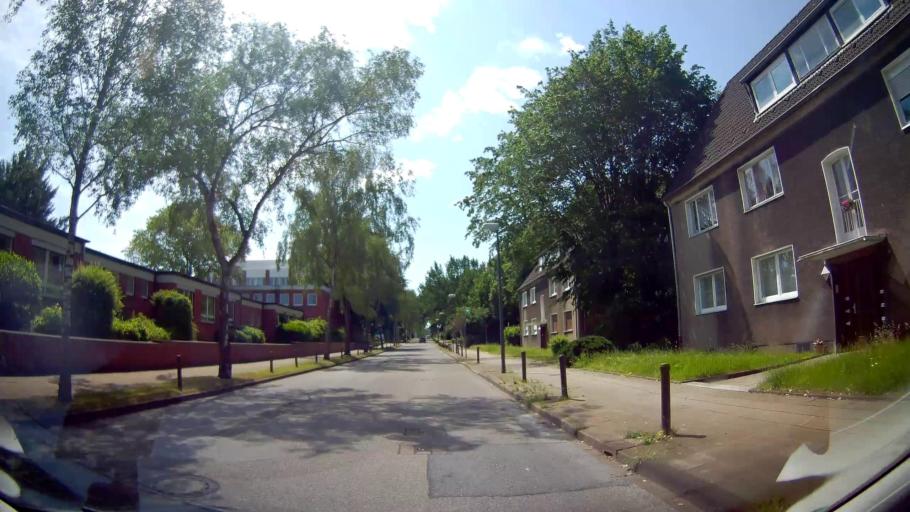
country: DE
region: North Rhine-Westphalia
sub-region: Regierungsbezirk Munster
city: Gladbeck
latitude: 51.5979
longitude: 7.0413
